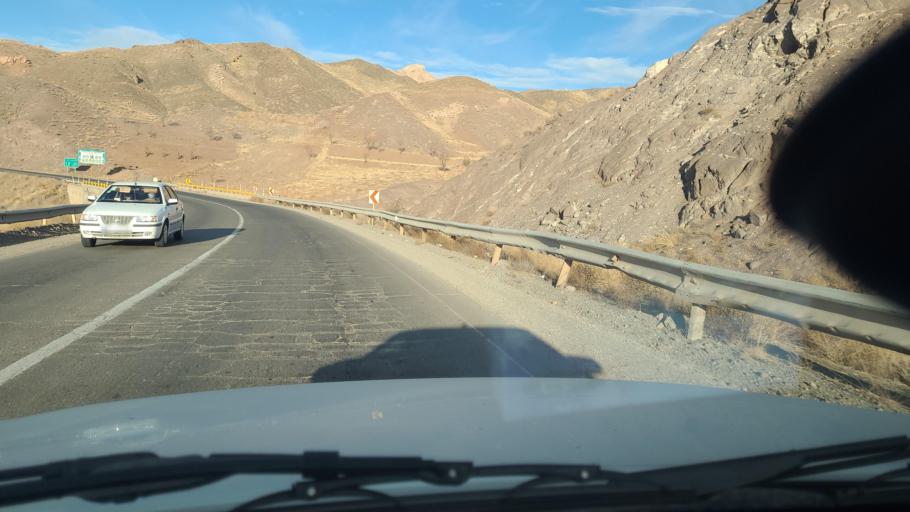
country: IR
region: Razavi Khorasan
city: Sabzevar
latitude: 36.4191
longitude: 57.5654
